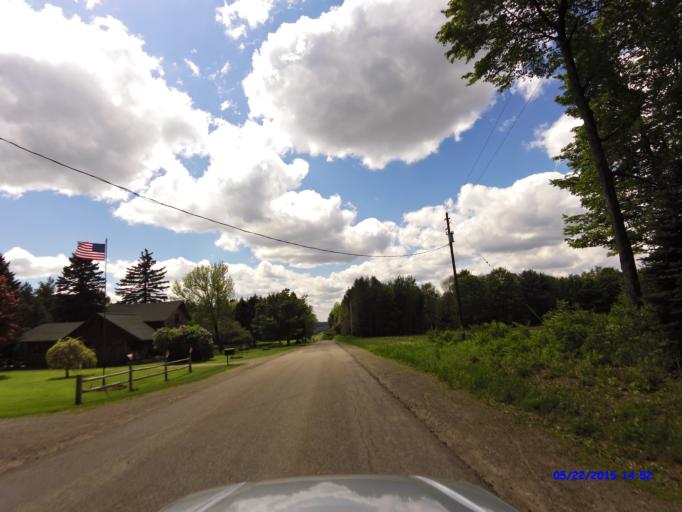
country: US
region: New York
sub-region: Cattaraugus County
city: Franklinville
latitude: 42.3818
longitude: -78.5749
